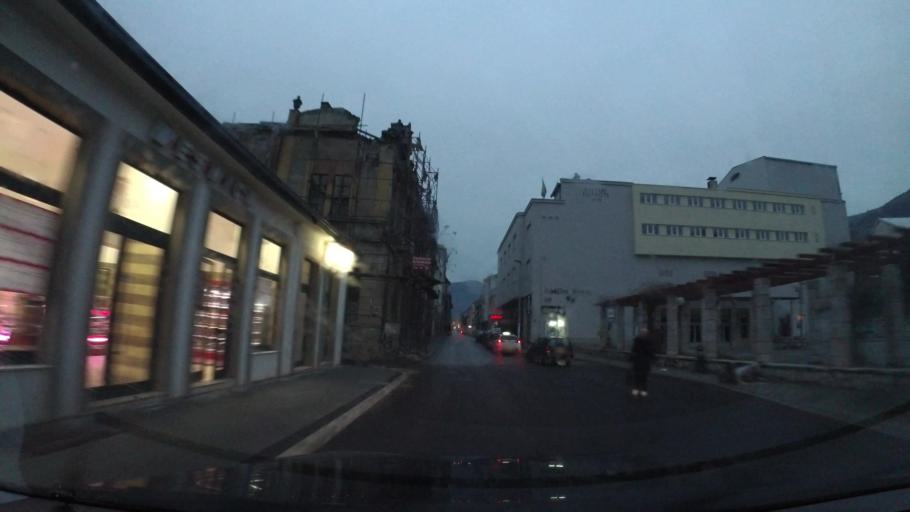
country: BA
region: Federation of Bosnia and Herzegovina
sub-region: Hercegovacko-Bosanski Kanton
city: Mostar
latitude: 43.3395
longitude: 17.8153
